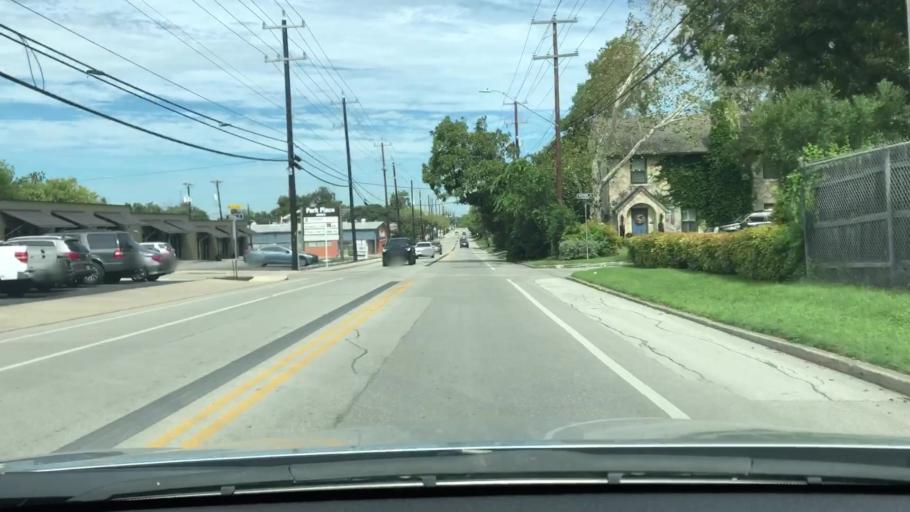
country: US
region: Texas
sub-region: Bexar County
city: Olmos Park
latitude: 29.4733
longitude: -98.4917
